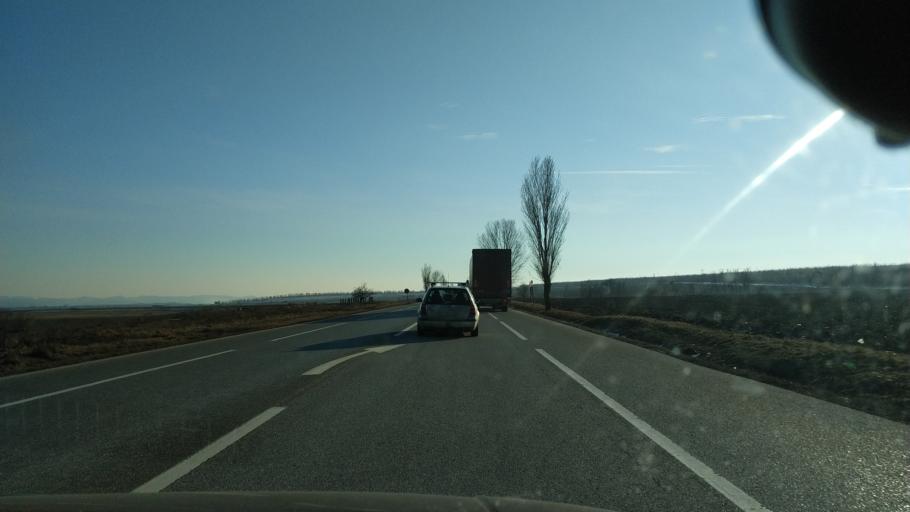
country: RO
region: Bacau
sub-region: Comuna Filipesti
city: Filipesti
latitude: 46.7222
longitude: 26.8888
